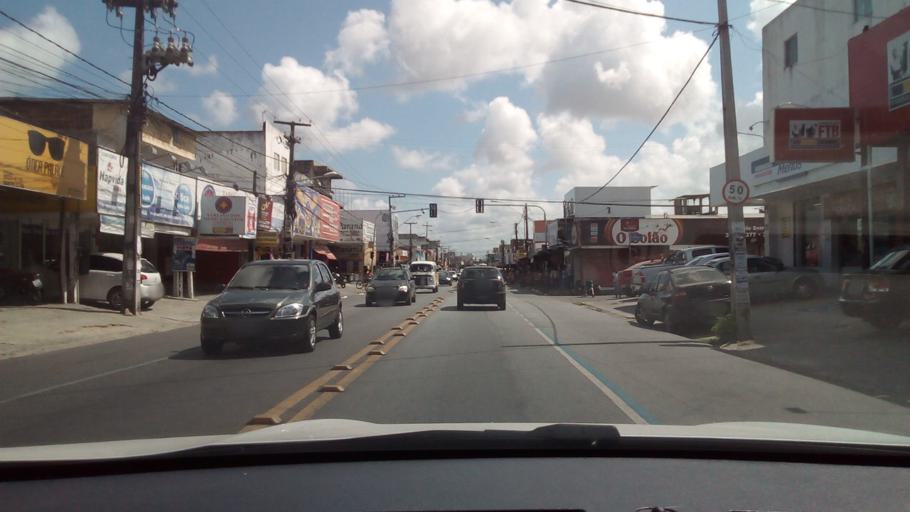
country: BR
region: Paraiba
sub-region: Joao Pessoa
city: Joao Pessoa
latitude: -7.1658
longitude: -34.8385
